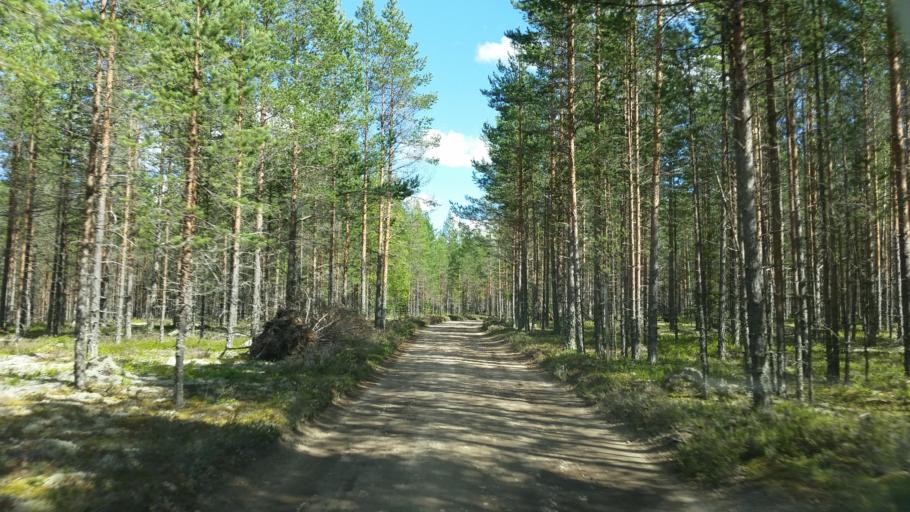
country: SE
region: Gaevleborg
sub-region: Ljusdals Kommun
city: Ljusdal
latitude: 61.9733
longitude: 16.2271
